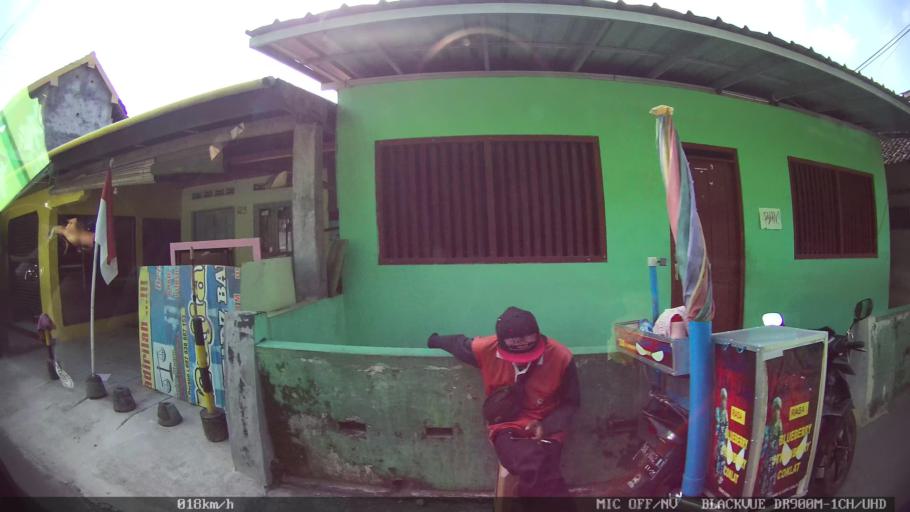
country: ID
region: Daerah Istimewa Yogyakarta
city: Kasihan
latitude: -7.8300
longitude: 110.3707
